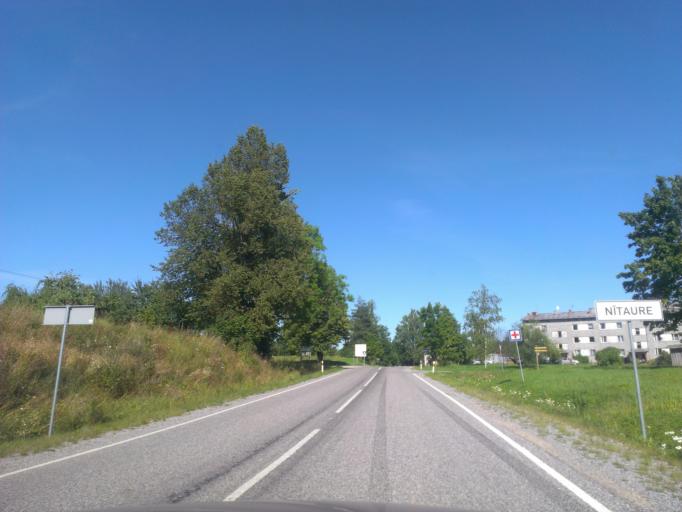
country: LV
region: Amatas Novads
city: Drabesi
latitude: 57.0665
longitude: 25.1874
